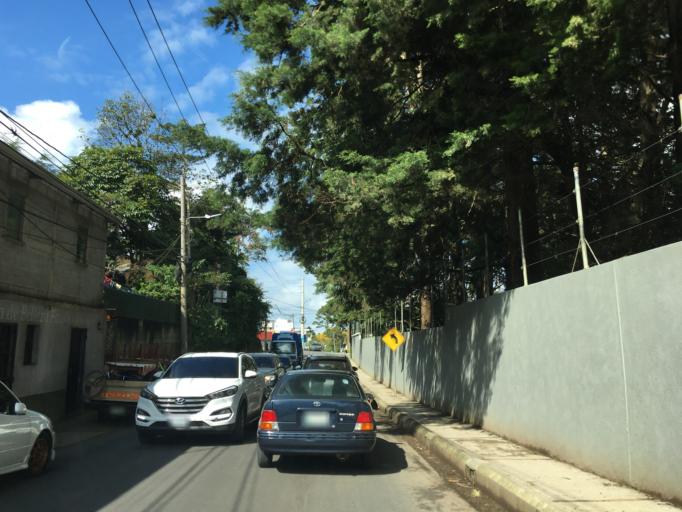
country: GT
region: Guatemala
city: San Jose Pinula
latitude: 14.5647
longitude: -90.4378
